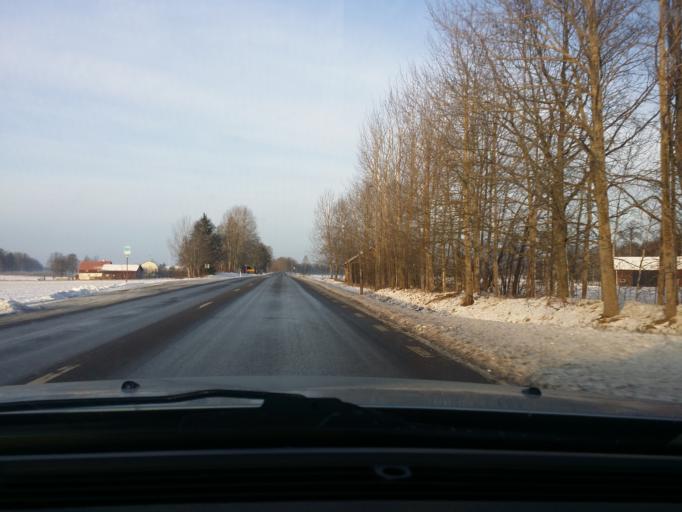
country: SE
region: OErebro
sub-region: Lindesbergs Kommun
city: Fellingsbro
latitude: 59.4631
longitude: 15.5621
